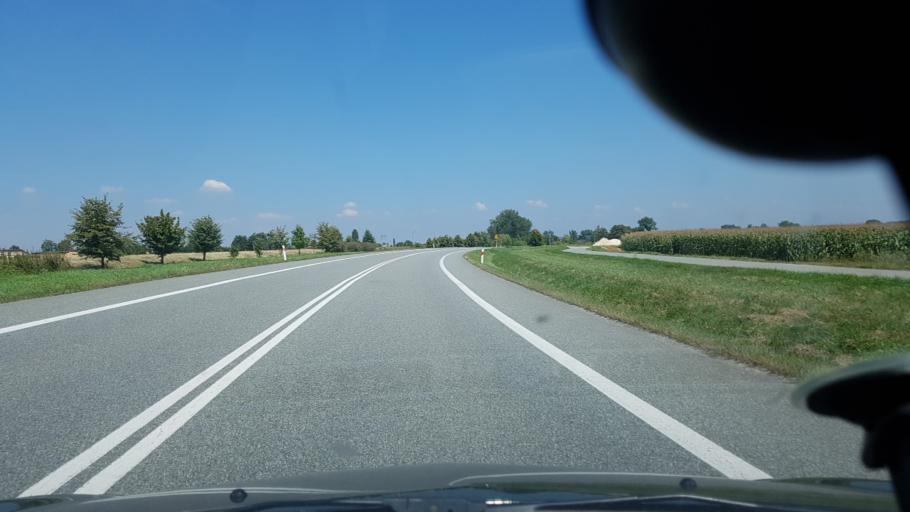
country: PL
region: Silesian Voivodeship
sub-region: Powiat raciborski
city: Chalupki
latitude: 49.9285
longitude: 18.3241
